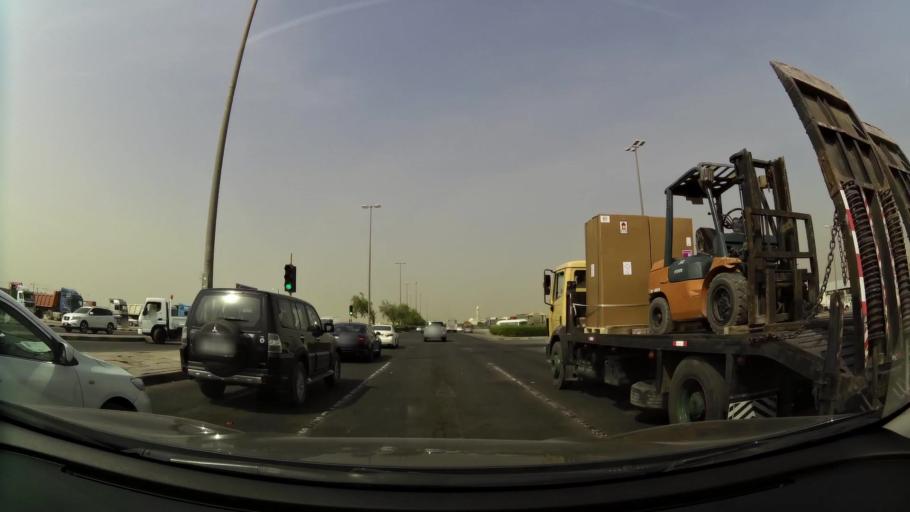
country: KW
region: Al Asimah
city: Ar Rabiyah
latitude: 29.2607
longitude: 47.9127
